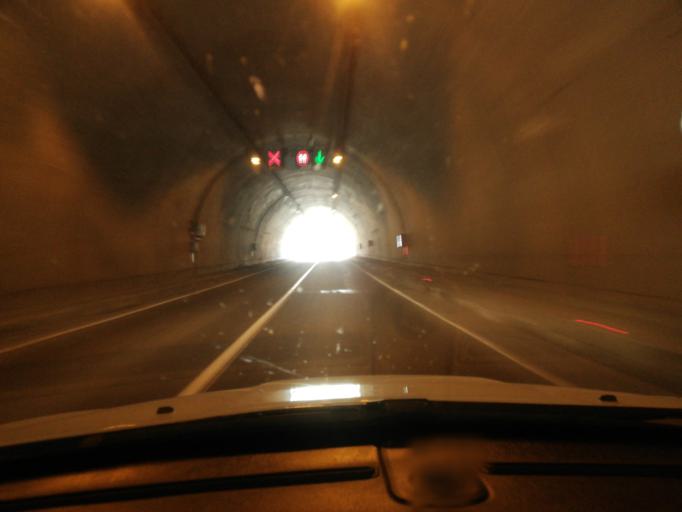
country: TR
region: Karabuk
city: Yenice
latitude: 41.1838
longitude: 32.4471
